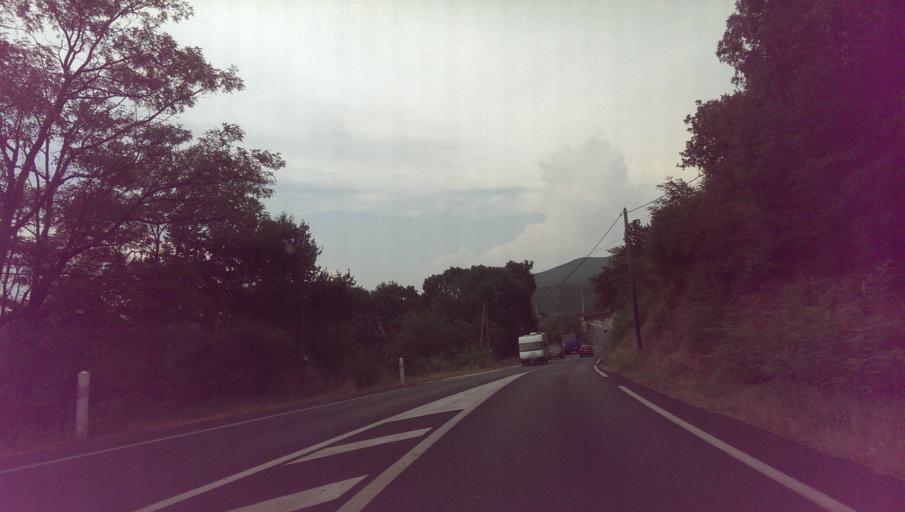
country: FR
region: Languedoc-Roussillon
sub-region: Departement des Pyrenees-Orientales
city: Vinca
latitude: 42.6513
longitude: 2.5543
